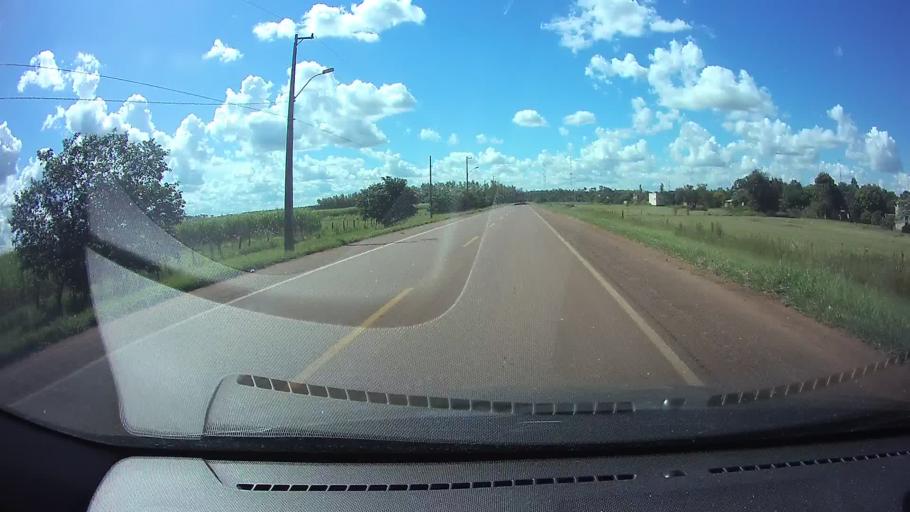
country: PY
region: Guaira
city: Coronel Martinez
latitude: -25.7818
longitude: -56.6495
